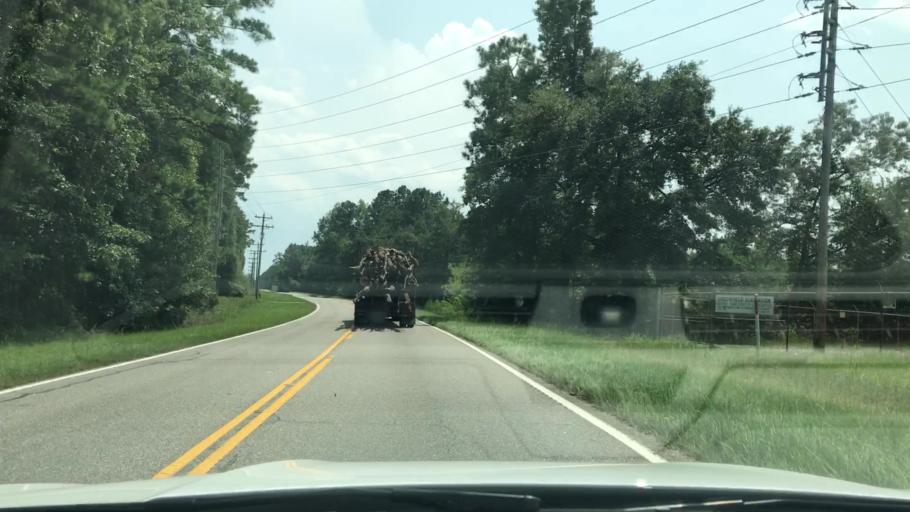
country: US
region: South Carolina
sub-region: Georgetown County
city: Georgetown
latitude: 33.4583
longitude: -79.2812
